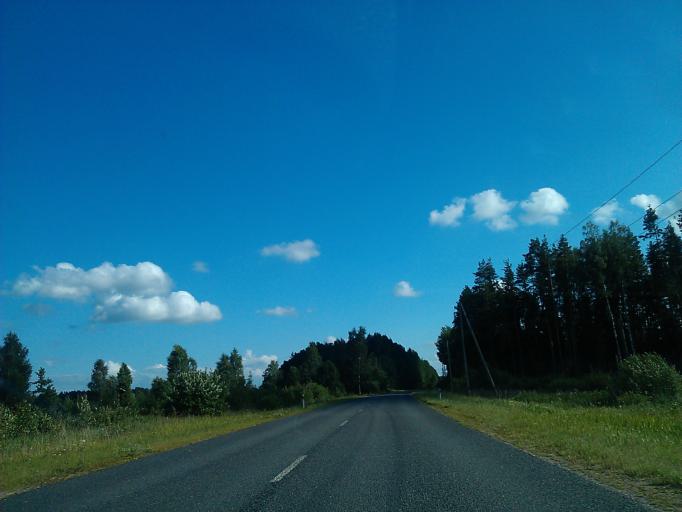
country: LV
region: Naukseni
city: Naukseni
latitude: 57.7740
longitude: 25.4316
